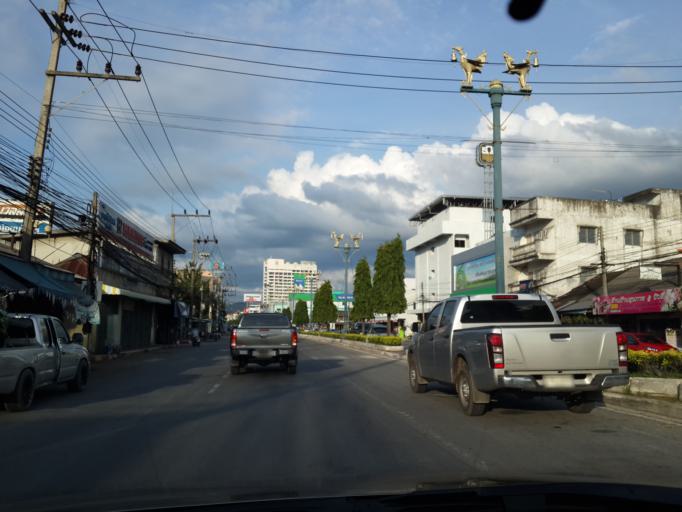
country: TH
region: Yala
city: Yala
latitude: 6.5531
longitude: 101.2829
